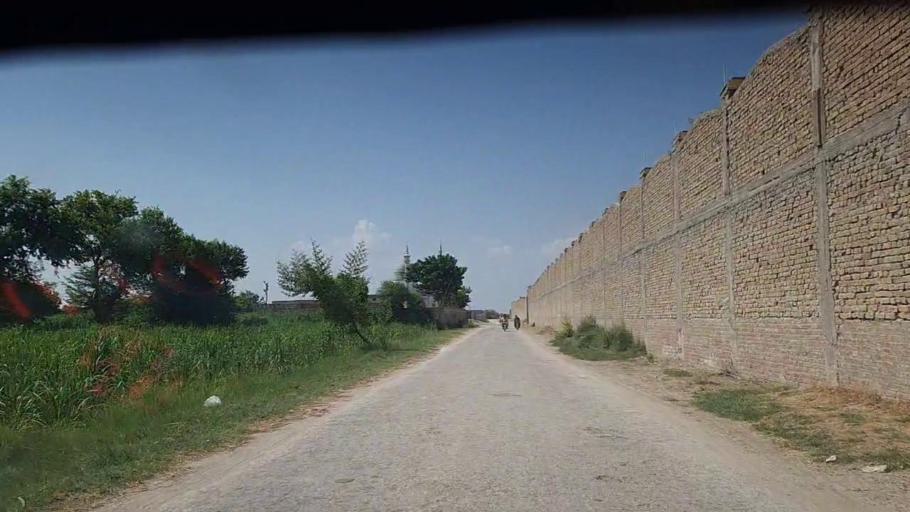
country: PK
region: Sindh
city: Khairpur
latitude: 28.0646
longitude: 69.6449
